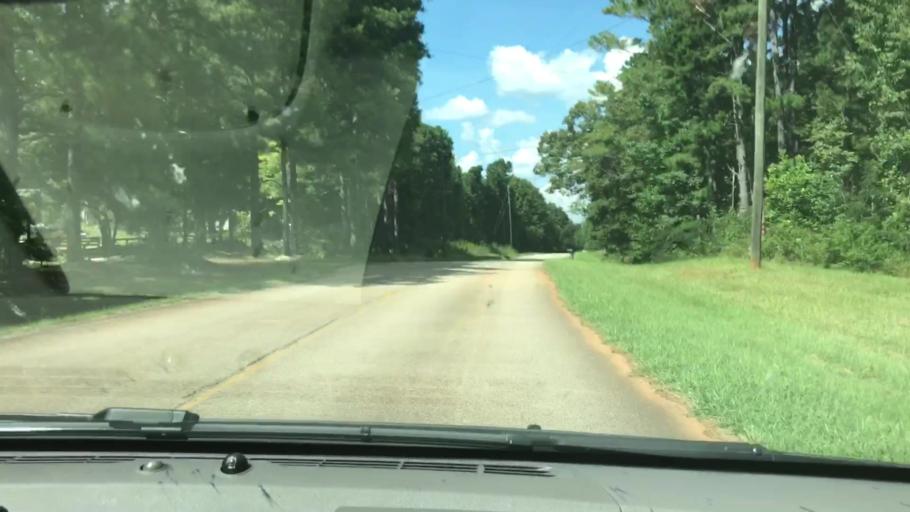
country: US
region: Georgia
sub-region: Troup County
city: La Grange
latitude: 33.0993
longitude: -85.1298
